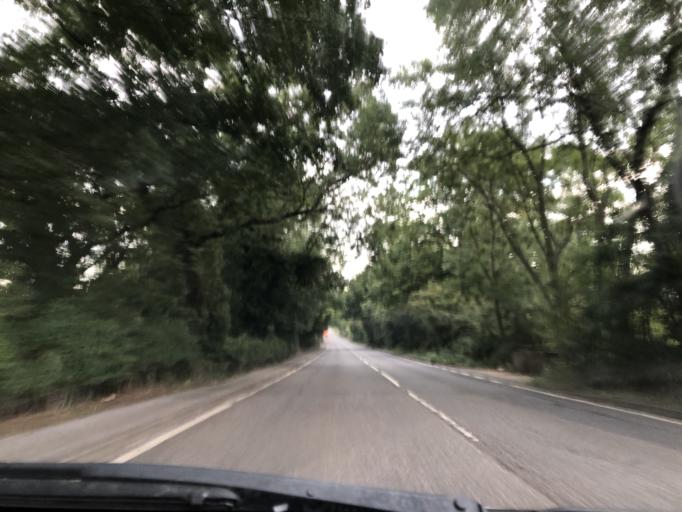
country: GB
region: England
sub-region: Kent
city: Sevenoaks
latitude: 51.2447
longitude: 0.2074
